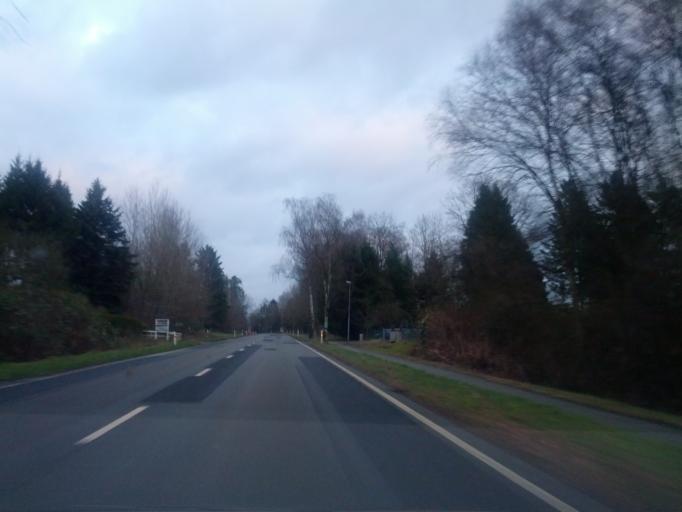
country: DE
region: Lower Saxony
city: Wistedt
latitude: 53.2653
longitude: 9.6705
